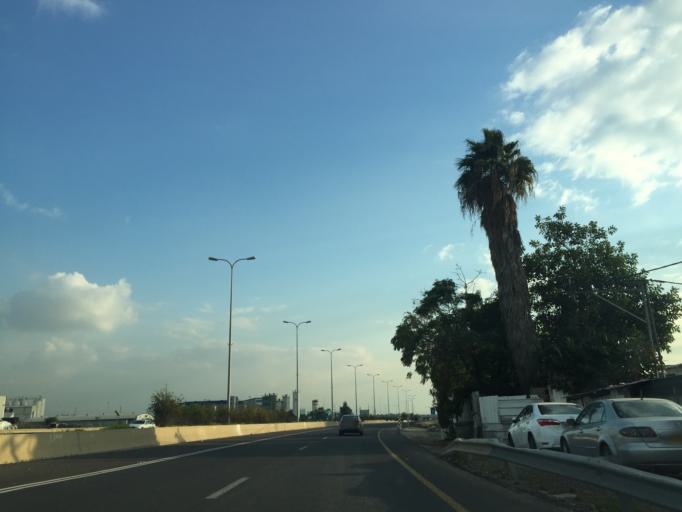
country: IL
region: Central District
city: Ramla
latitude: 31.9222
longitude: 34.8848
